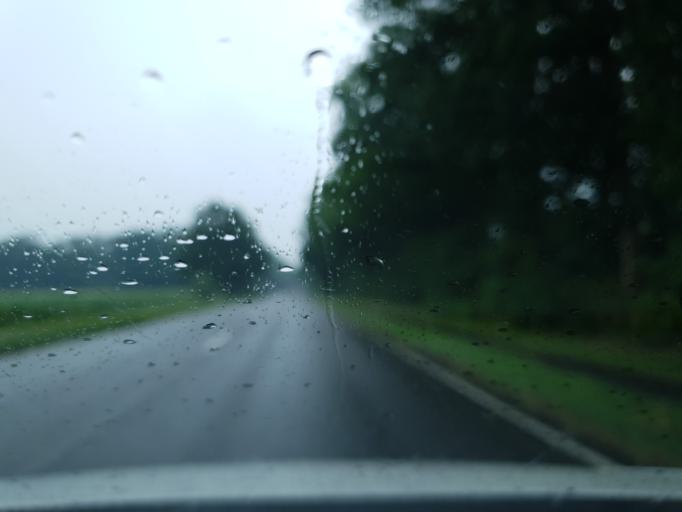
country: DE
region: Lower Saxony
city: Lingen
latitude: 52.5463
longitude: 7.2932
